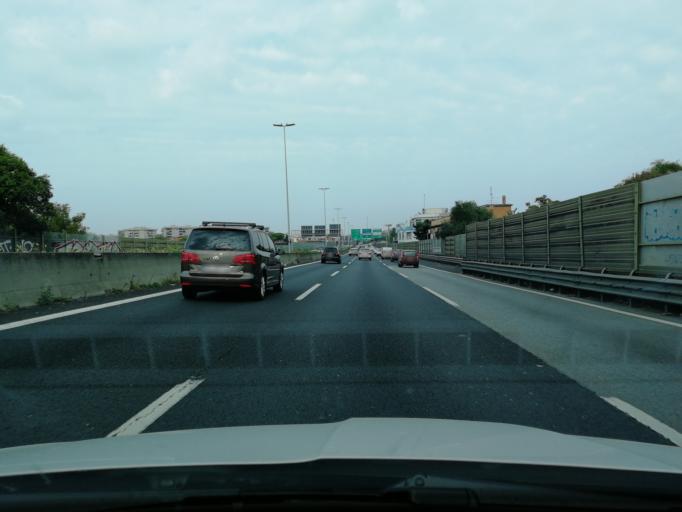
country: IT
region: Latium
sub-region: Citta metropolitana di Roma Capitale
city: Ciampino
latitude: 41.8420
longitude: 12.5928
